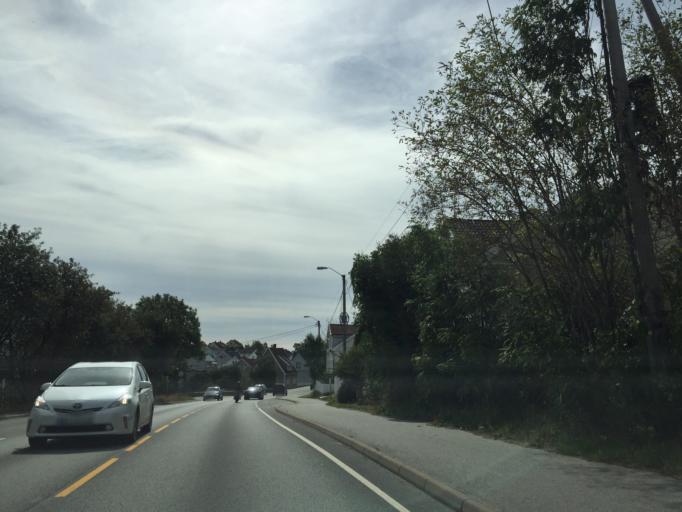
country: NO
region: Ostfold
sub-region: Fredrikstad
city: Fredrikstad
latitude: 59.1981
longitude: 10.9415
